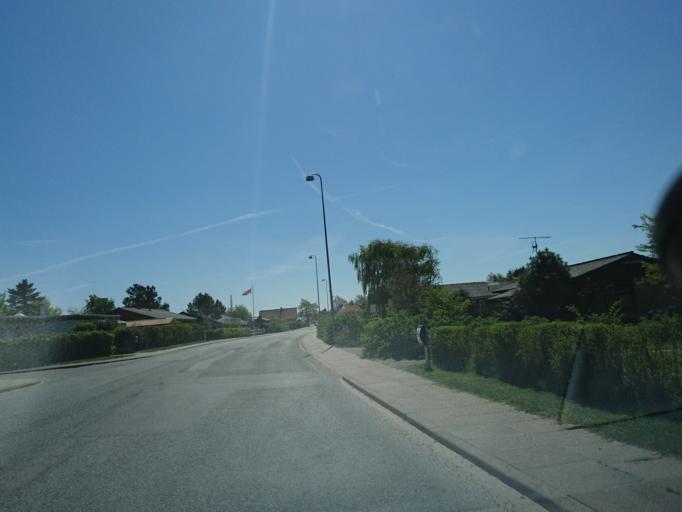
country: DK
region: North Denmark
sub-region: Hjorring Kommune
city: Sindal
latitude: 57.5892
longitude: 10.1876
